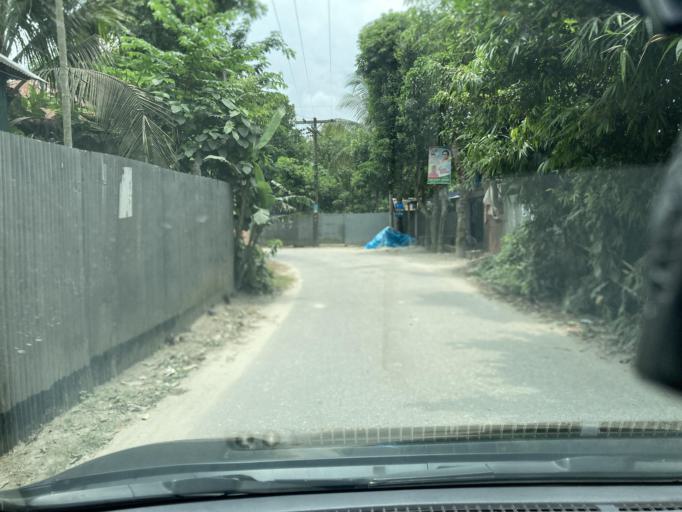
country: BD
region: Dhaka
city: Dohar
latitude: 23.8091
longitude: 90.0453
